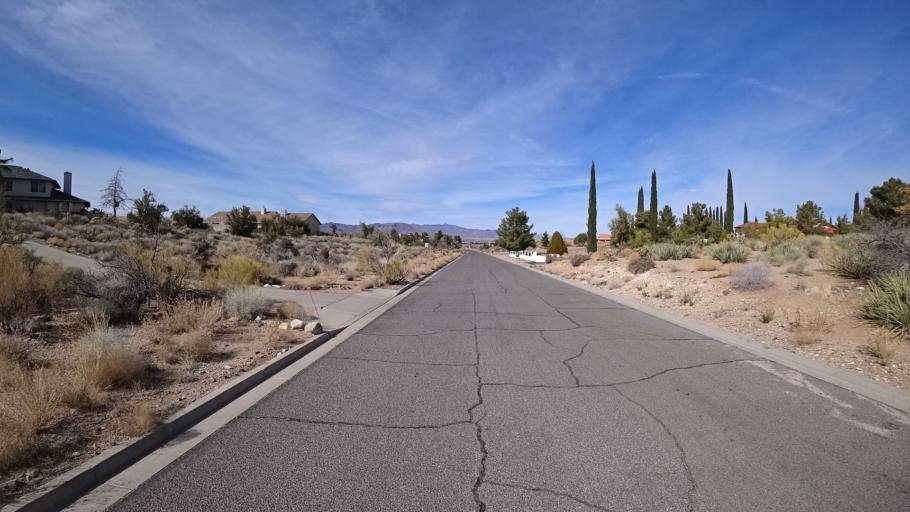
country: US
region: Arizona
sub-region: Mohave County
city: Kingman
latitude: 35.1857
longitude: -113.9874
